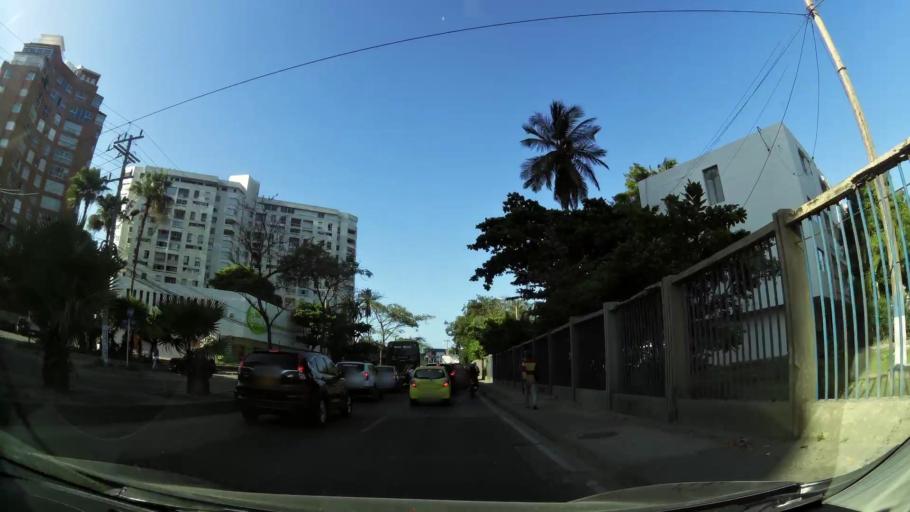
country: CO
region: Bolivar
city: Cartagena
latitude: 10.4128
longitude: -75.5503
